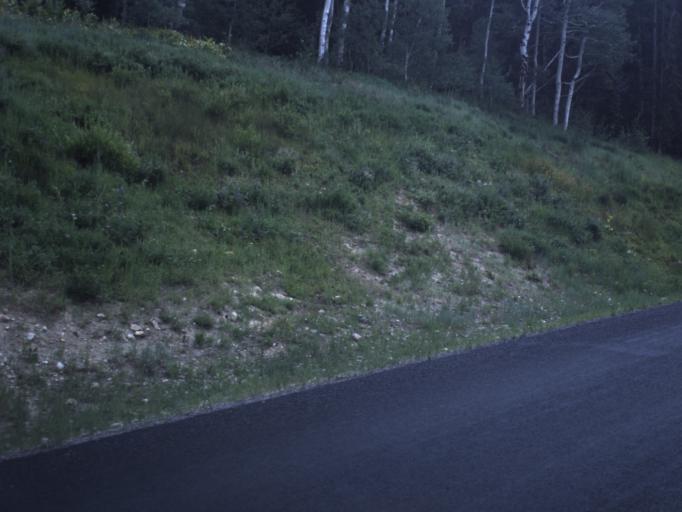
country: US
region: Utah
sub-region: Summit County
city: Francis
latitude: 40.4928
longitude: -111.0346
